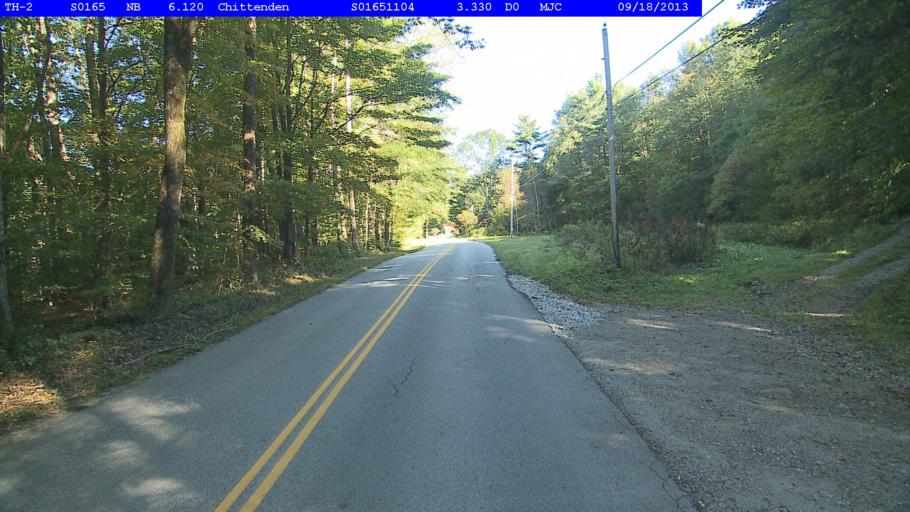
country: US
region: Vermont
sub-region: Rutland County
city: Rutland
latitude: 43.7225
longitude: -72.9671
